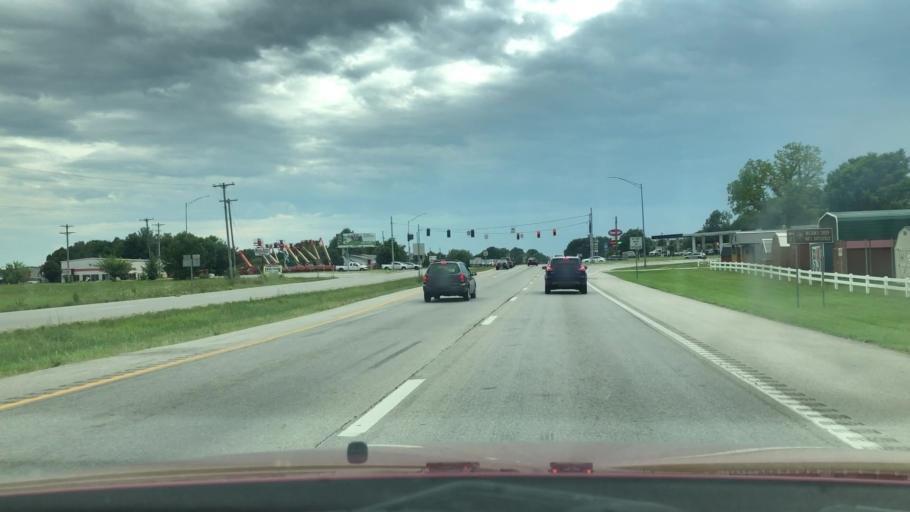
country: US
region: Missouri
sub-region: Greene County
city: Republic
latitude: 37.1467
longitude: -93.4277
